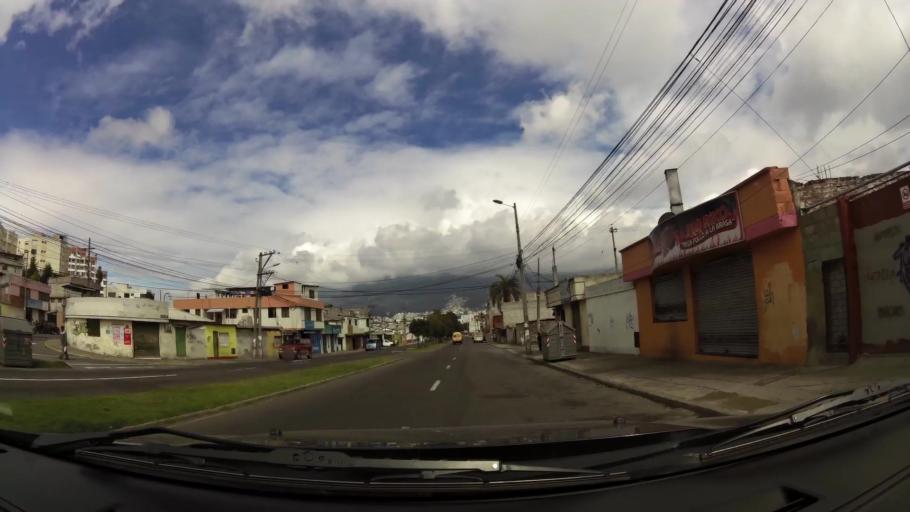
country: EC
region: Pichincha
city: Quito
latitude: -0.1536
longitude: -78.4674
